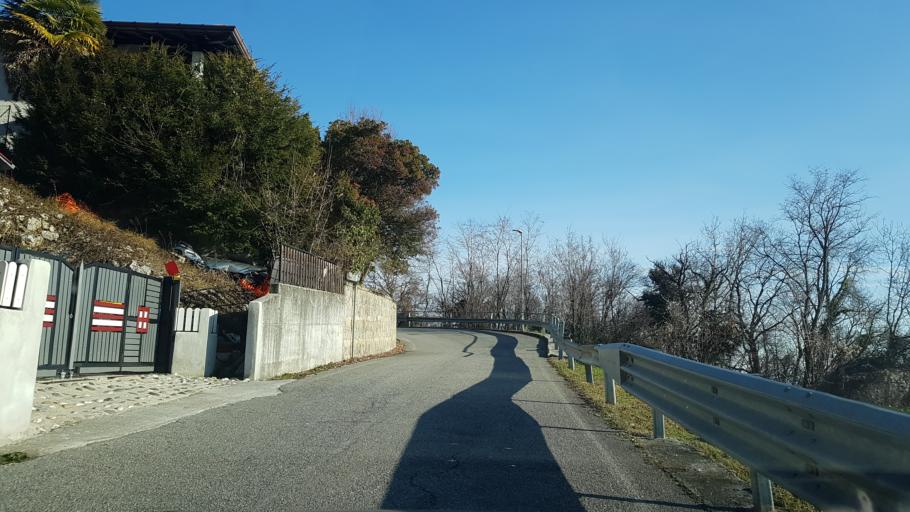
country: IT
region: Friuli Venezia Giulia
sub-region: Provincia di Udine
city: Forgaria nel Friuli
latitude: 46.2267
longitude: 12.9950
